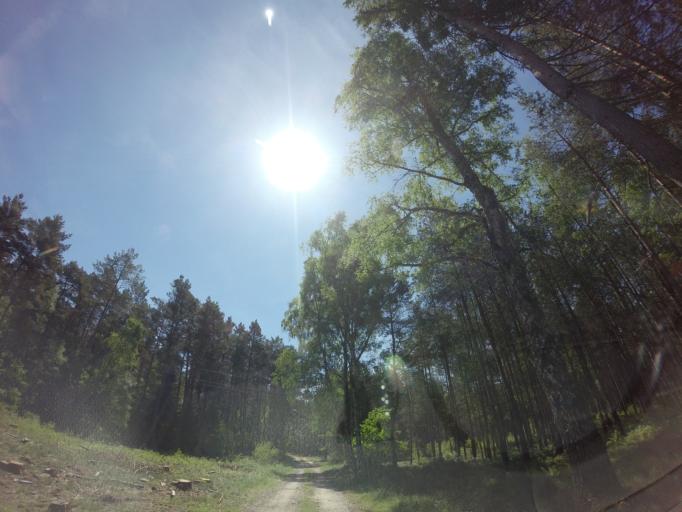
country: PL
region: West Pomeranian Voivodeship
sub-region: Powiat choszczenski
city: Drawno
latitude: 53.2583
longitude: 15.7470
